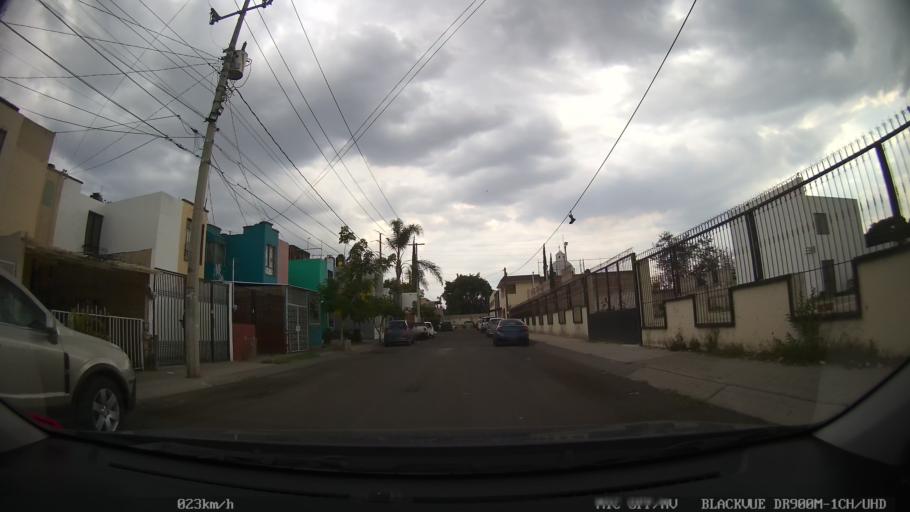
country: MX
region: Jalisco
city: Tlaquepaque
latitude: 20.6243
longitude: -103.2773
